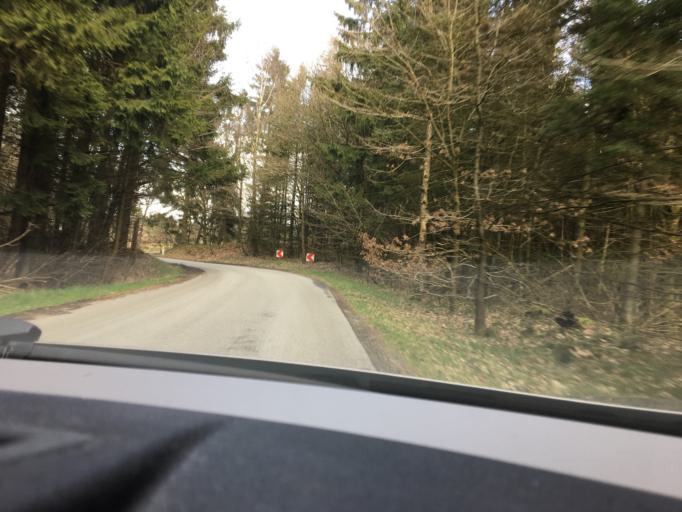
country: DK
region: South Denmark
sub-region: Vejle Kommune
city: Give
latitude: 55.8276
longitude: 9.3101
